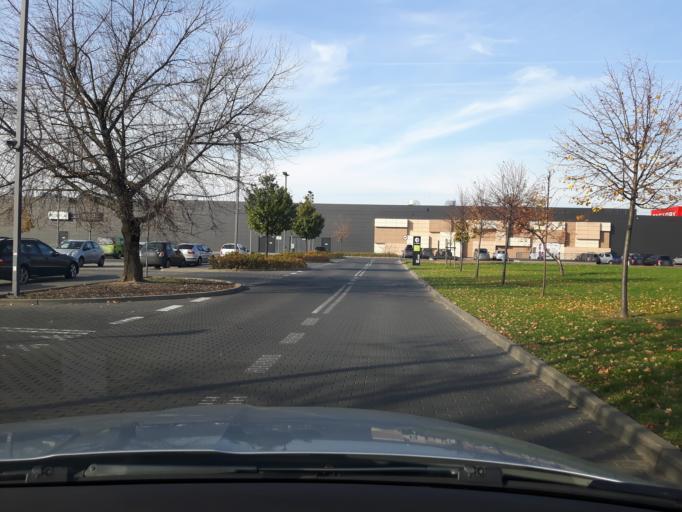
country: PL
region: Masovian Voivodeship
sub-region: Warszawa
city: Targowek
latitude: 52.2990
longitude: 21.0270
